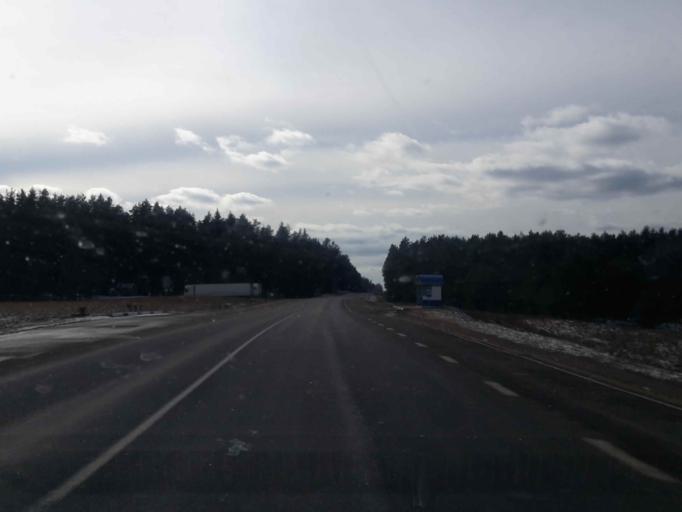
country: BY
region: Minsk
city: Myadzyel
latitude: 55.0486
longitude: 27.0860
